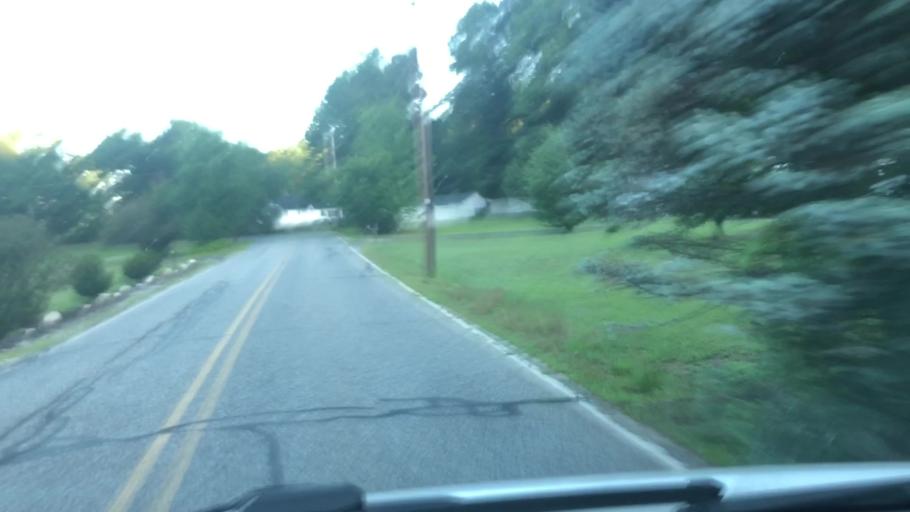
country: US
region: Massachusetts
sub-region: Hampshire County
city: Easthampton
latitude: 42.2404
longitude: -72.6942
